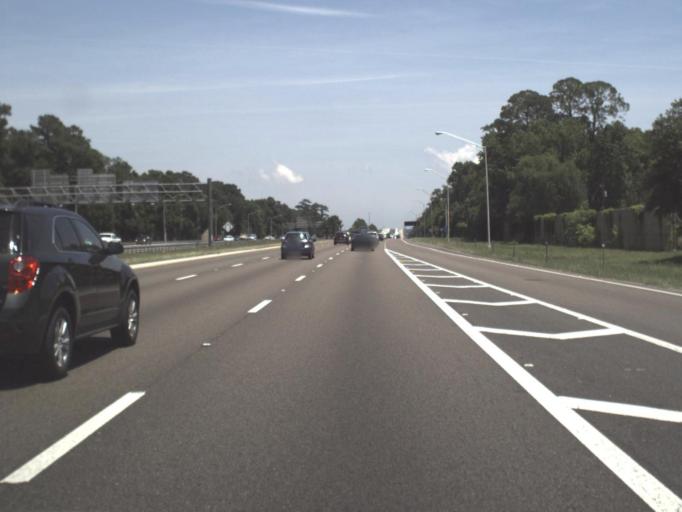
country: US
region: Florida
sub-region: Clay County
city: Orange Park
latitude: 30.1915
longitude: -81.7004
